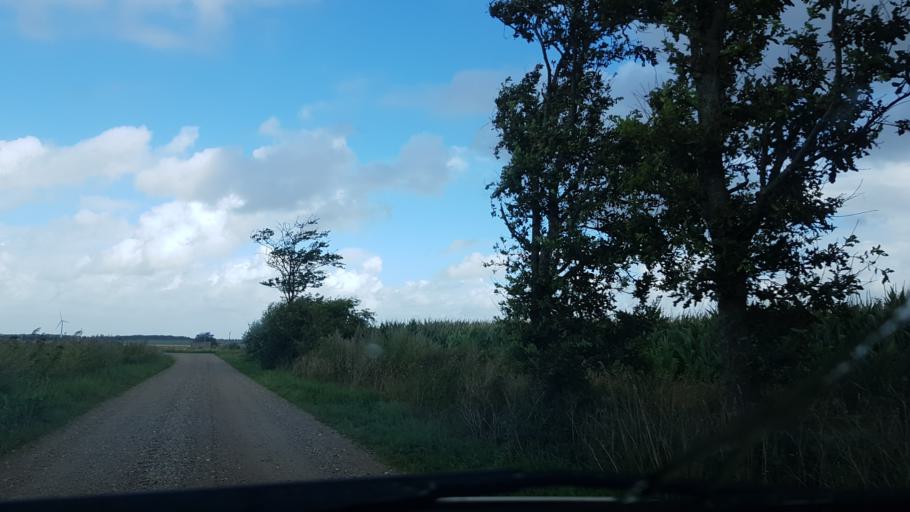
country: DK
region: South Denmark
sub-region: Tonder Kommune
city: Sherrebek
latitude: 55.2277
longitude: 8.7846
